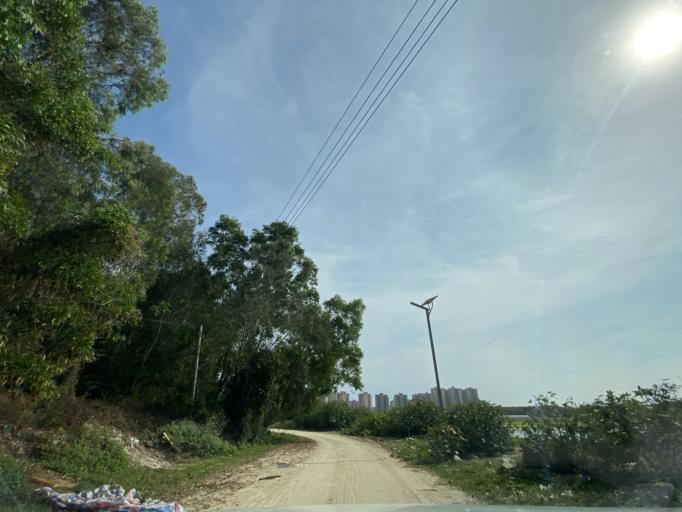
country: CN
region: Hainan
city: Yingzhou
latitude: 18.4078
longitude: 109.8357
